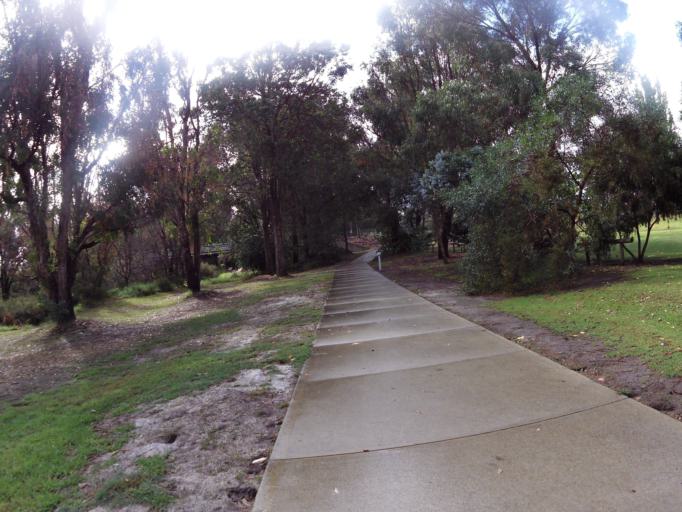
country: AU
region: Western Australia
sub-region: Donnybrook-Balingup
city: Donnybrook
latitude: -33.5720
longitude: 115.8259
